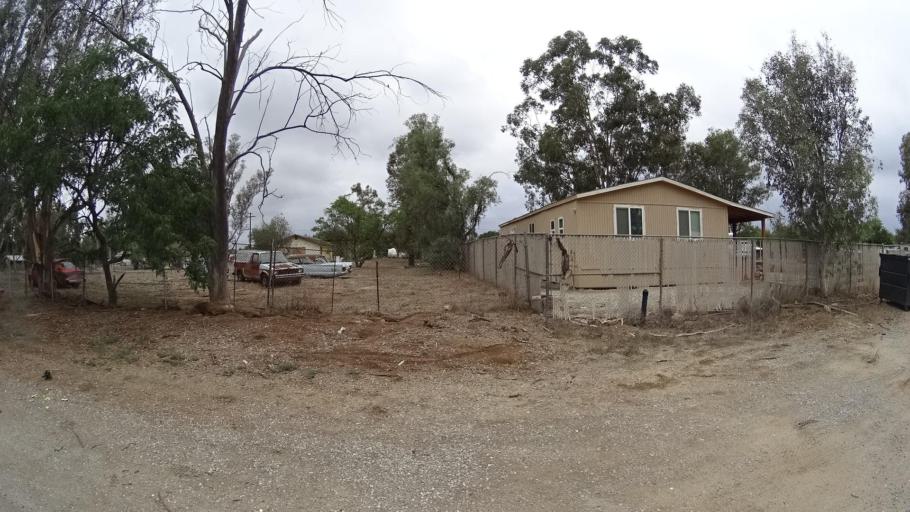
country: US
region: California
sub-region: San Diego County
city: Ramona
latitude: 33.0297
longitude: -116.8892
